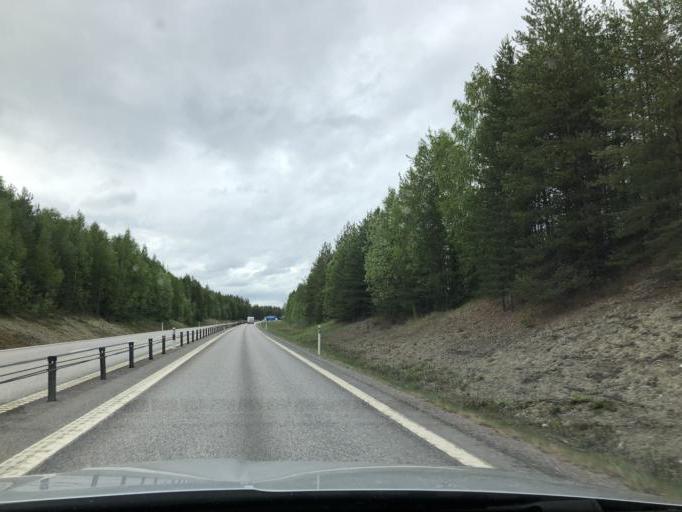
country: SE
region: Norrbotten
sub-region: Pitea Kommun
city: Bergsviken
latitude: 65.3014
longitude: 21.4143
